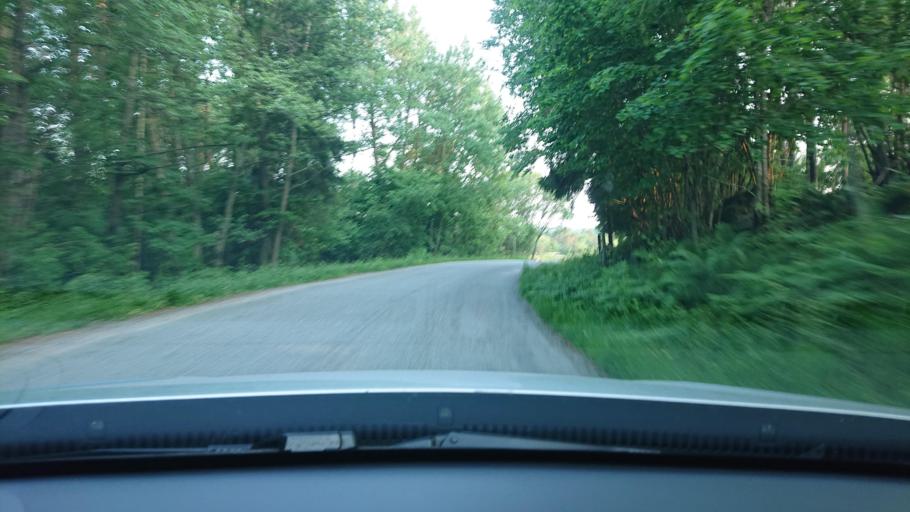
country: SE
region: Stockholm
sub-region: Osterakers Kommun
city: Akersberga
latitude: 59.5113
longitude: 18.3155
